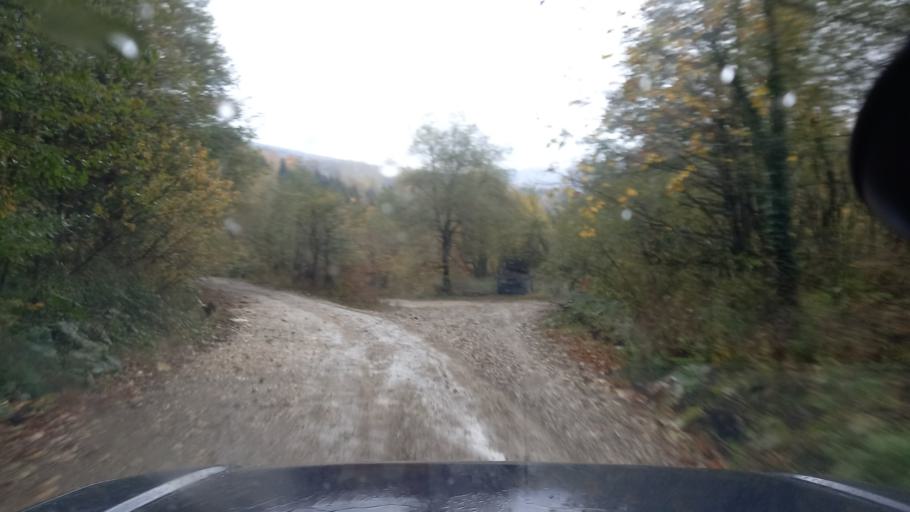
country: RU
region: Krasnodarskiy
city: Neftegorsk
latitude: 44.0351
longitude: 39.8361
